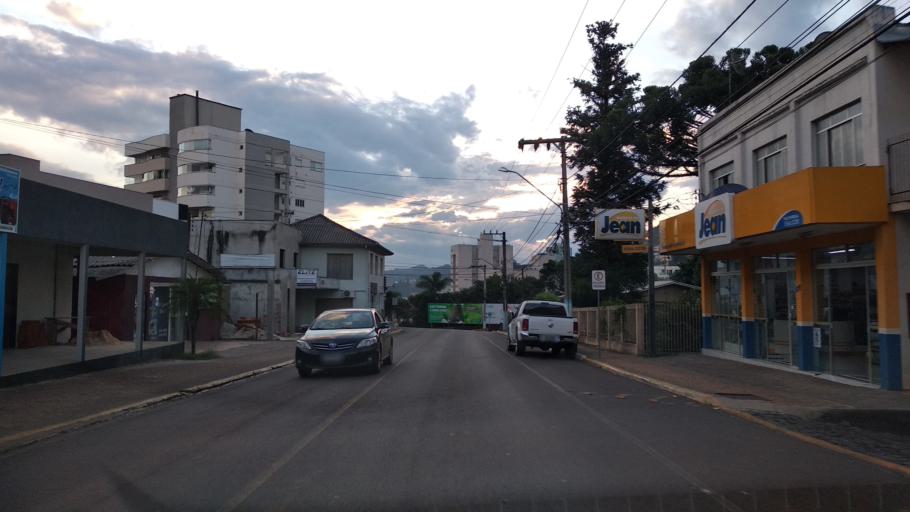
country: BR
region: Santa Catarina
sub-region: Videira
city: Videira
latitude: -27.0055
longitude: -51.1459
